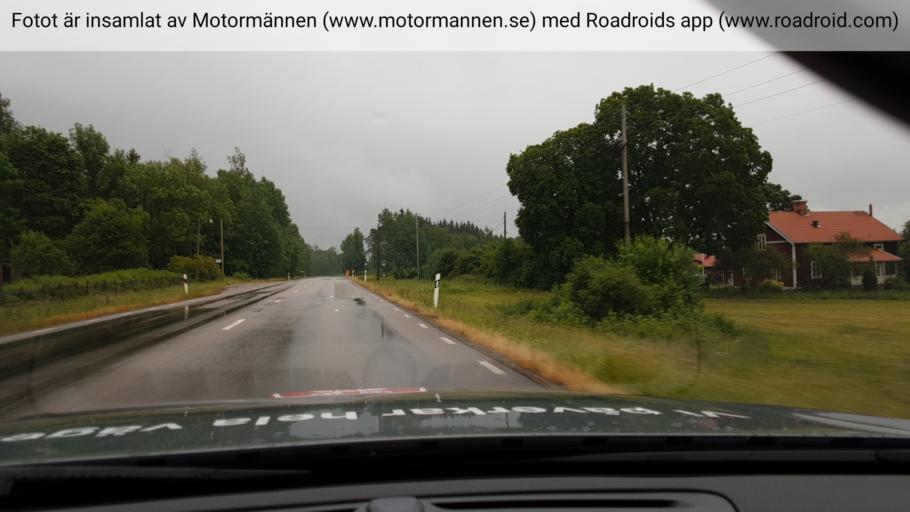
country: SE
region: Vaestmanland
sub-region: Norbergs Kommun
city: Norberg
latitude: 60.0324
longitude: 15.9890
